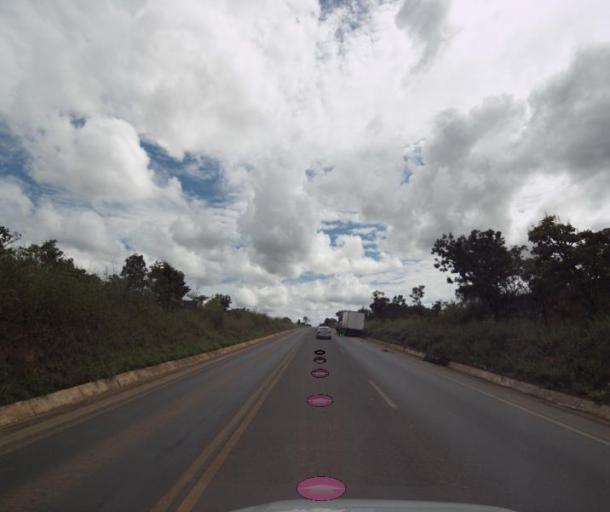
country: BR
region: Goias
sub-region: Uruacu
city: Uruacu
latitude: -14.4820
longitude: -49.1538
